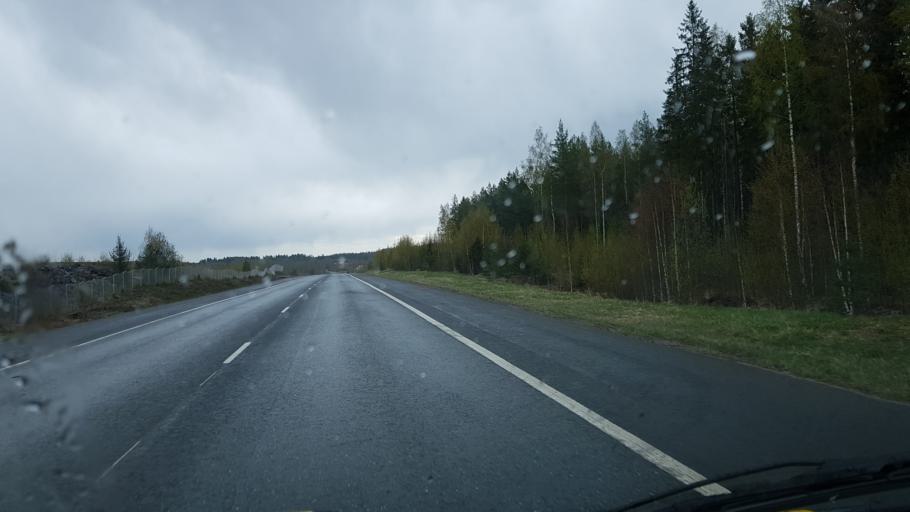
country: FI
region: Pirkanmaa
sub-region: Tampere
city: Pirkkala
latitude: 61.4148
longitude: 23.6342
